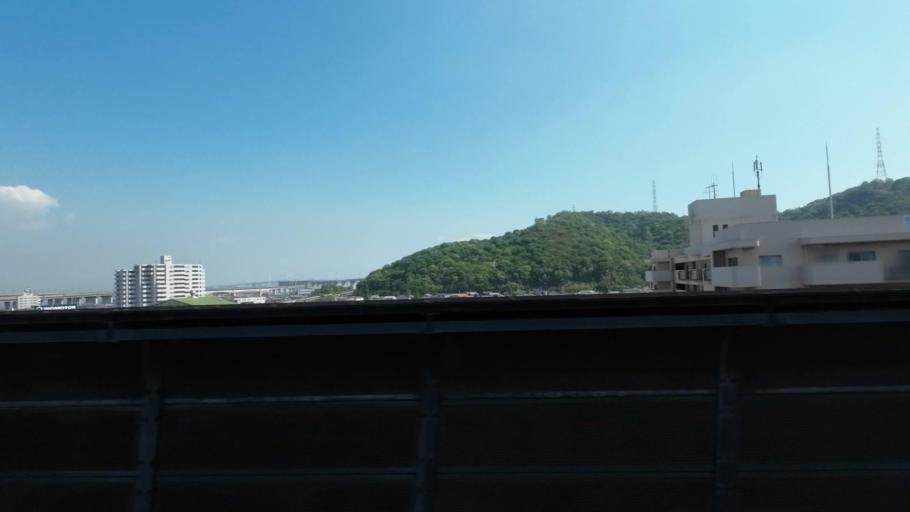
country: JP
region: Kagawa
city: Sakaidecho
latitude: 34.3133
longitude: 133.8264
